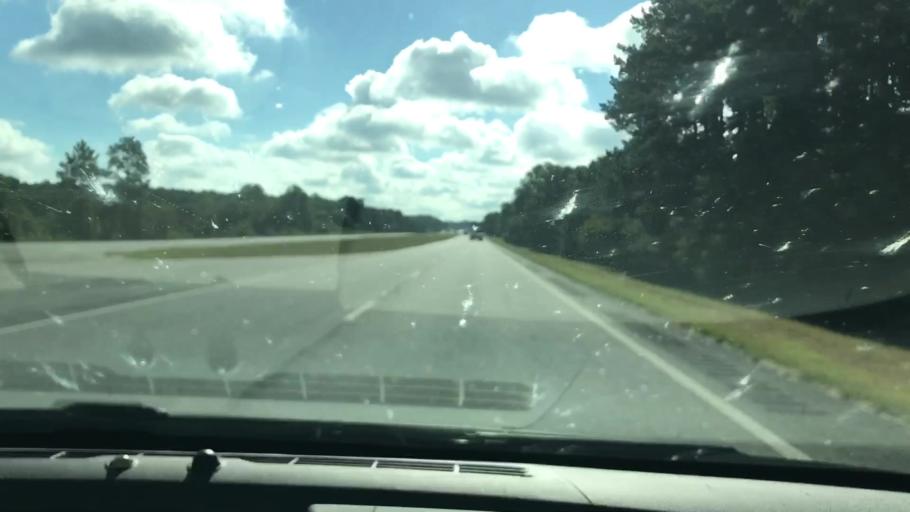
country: US
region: Georgia
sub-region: Worth County
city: Sylvester
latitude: 31.5541
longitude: -83.9868
